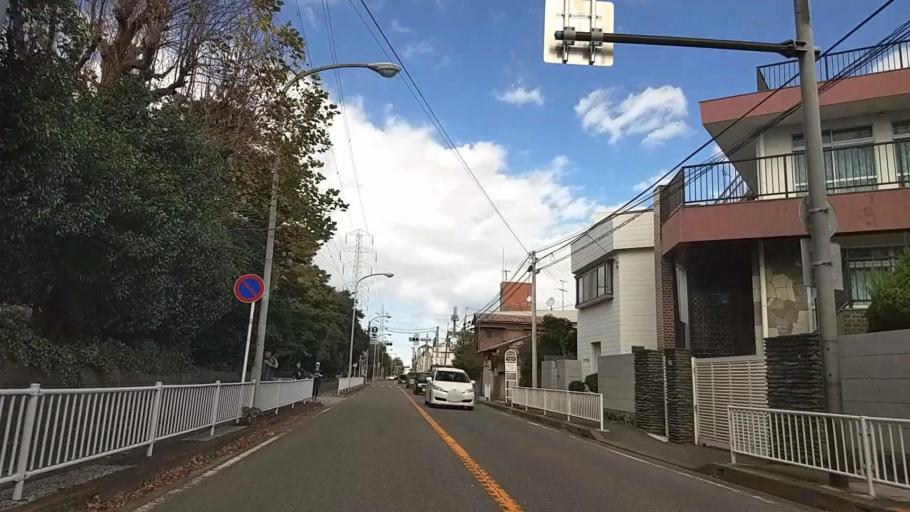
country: JP
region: Kanagawa
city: Yokohama
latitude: 35.4960
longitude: 139.6369
